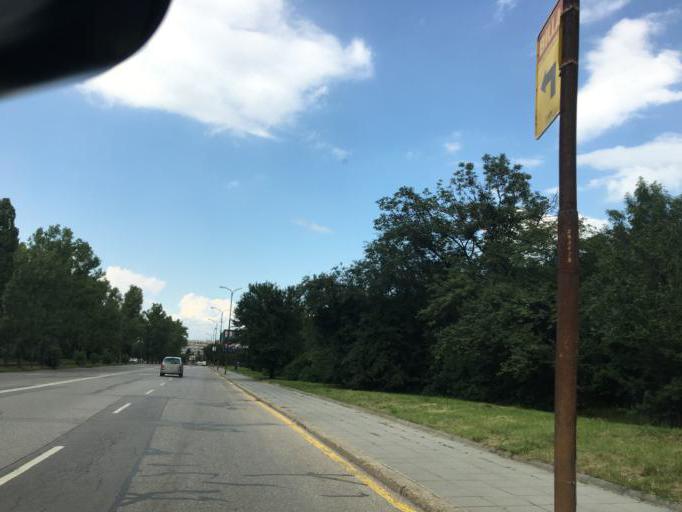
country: BG
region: Sofia-Capital
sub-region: Stolichna Obshtina
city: Sofia
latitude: 42.6585
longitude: 23.3591
